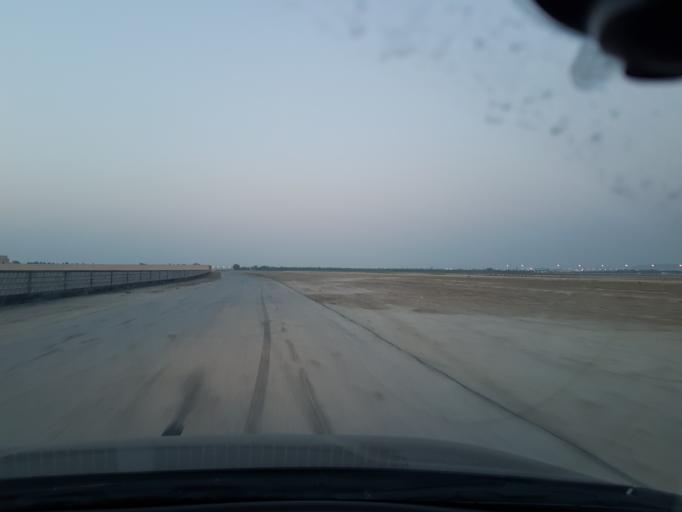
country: BH
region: Central Governorate
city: Dar Kulayb
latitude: 26.0035
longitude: 50.4738
